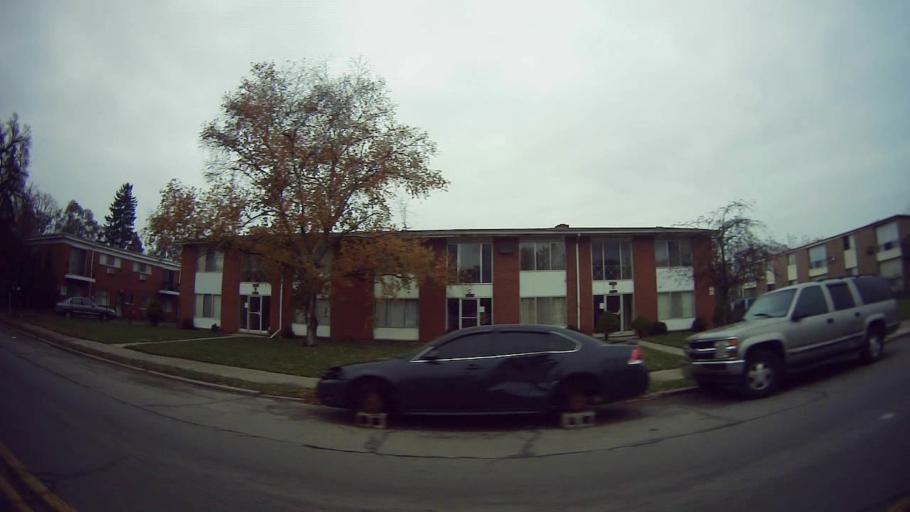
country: US
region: Michigan
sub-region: Wayne County
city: Redford
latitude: 42.4134
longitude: -83.2574
